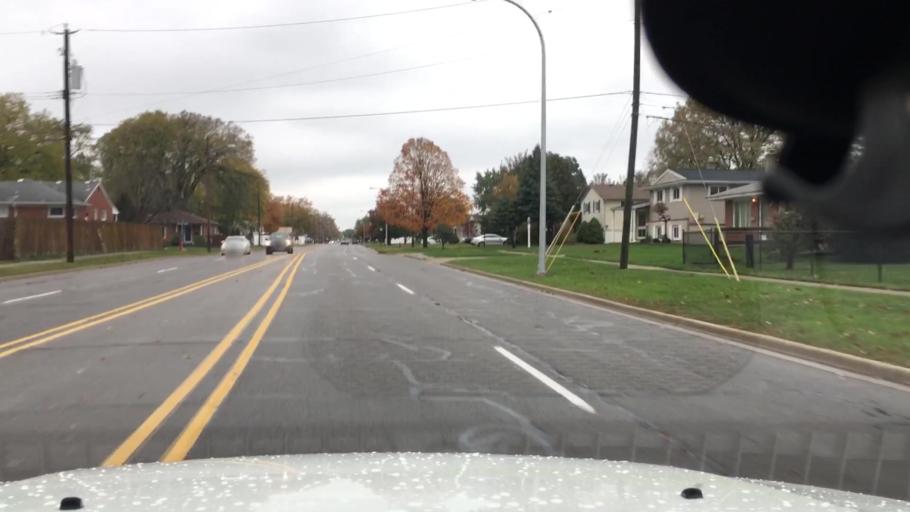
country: US
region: Michigan
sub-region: Oakland County
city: Clawson
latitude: 42.5205
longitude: -83.1257
